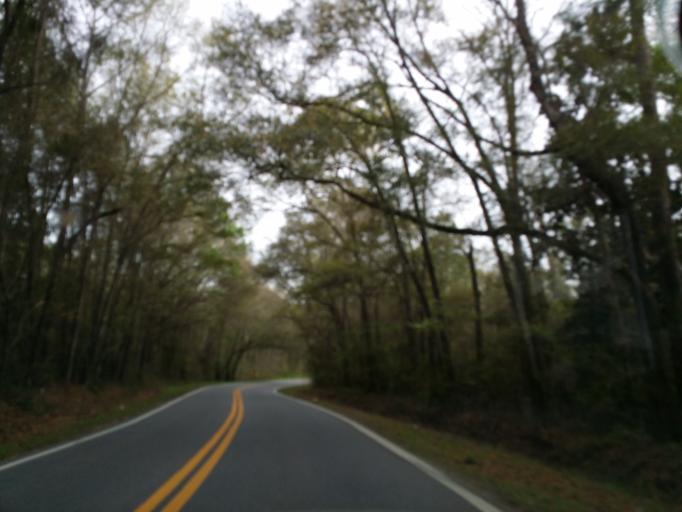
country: US
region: Florida
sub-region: Leon County
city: Tallahassee
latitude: 30.5071
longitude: -84.1252
